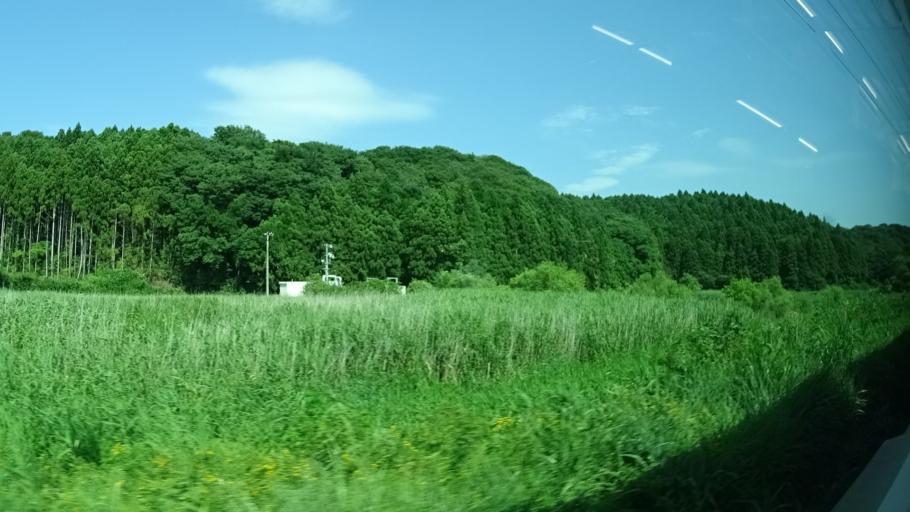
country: JP
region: Miyagi
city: Kogota
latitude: 38.4969
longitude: 141.0869
